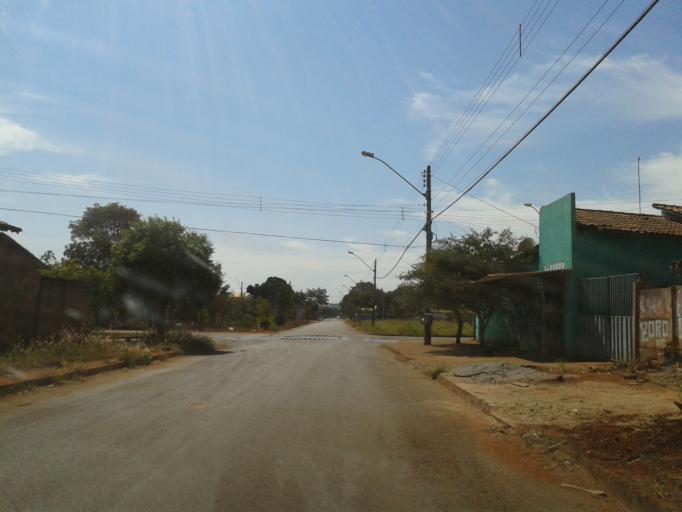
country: BR
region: Goias
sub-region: Goiania
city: Goiania
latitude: -16.6510
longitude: -49.3495
